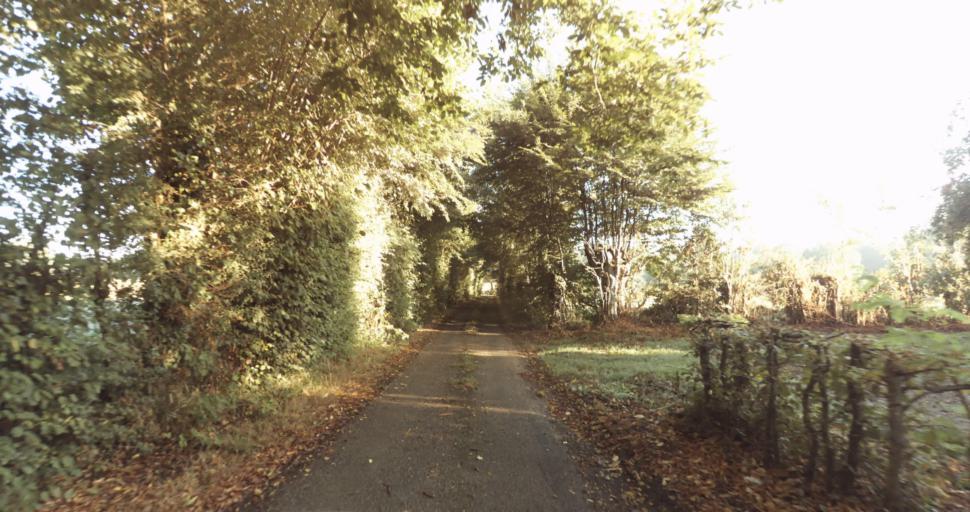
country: FR
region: Lower Normandy
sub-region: Departement de l'Orne
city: Vimoutiers
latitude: 48.9135
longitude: 0.1569
